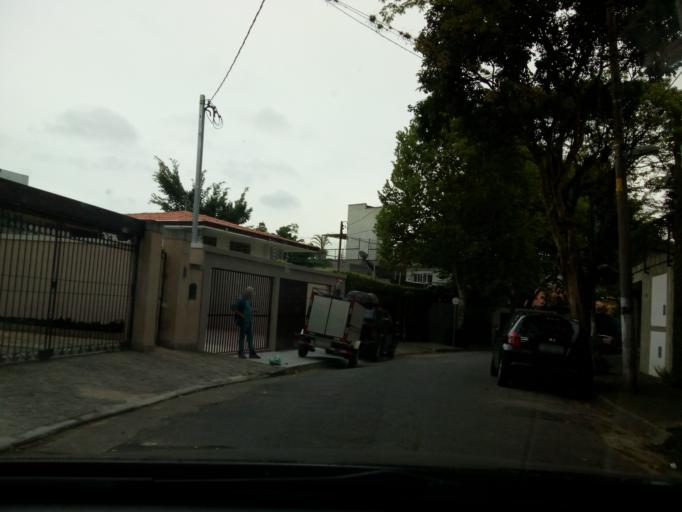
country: BR
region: Sao Paulo
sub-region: Sao Paulo
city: Sao Paulo
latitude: -23.5496
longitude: -46.6692
